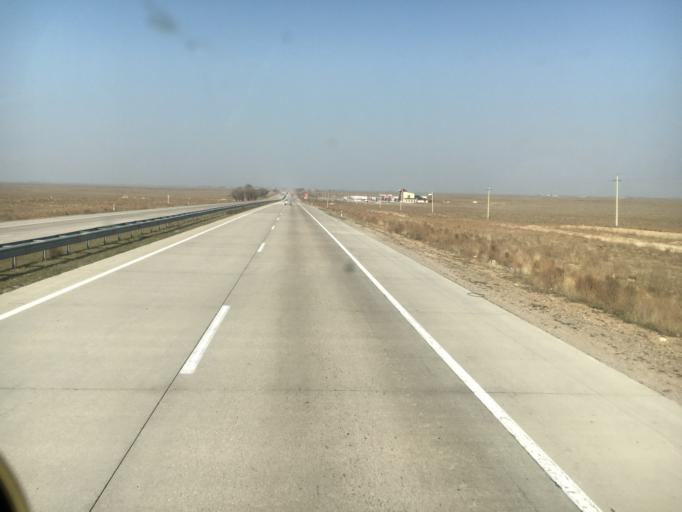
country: KZ
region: Ongtustik Qazaqstan
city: Temirlanovka
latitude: 42.8375
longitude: 69.1130
